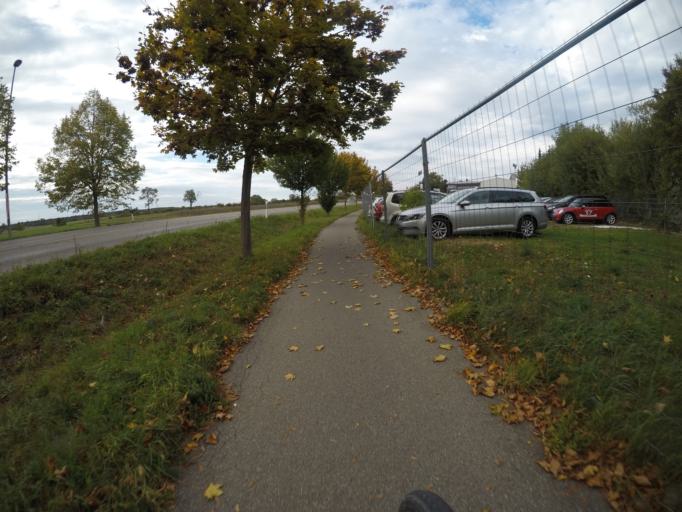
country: DE
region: Baden-Wuerttemberg
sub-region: Regierungsbezirk Stuttgart
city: Nufringen
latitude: 48.6270
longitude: 8.8937
